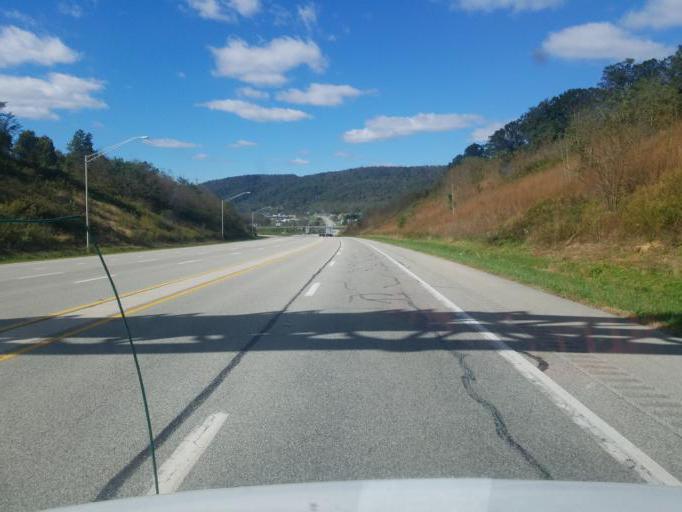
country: US
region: Pennsylvania
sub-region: Bedford County
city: Everett
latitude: 40.0238
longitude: -78.4293
